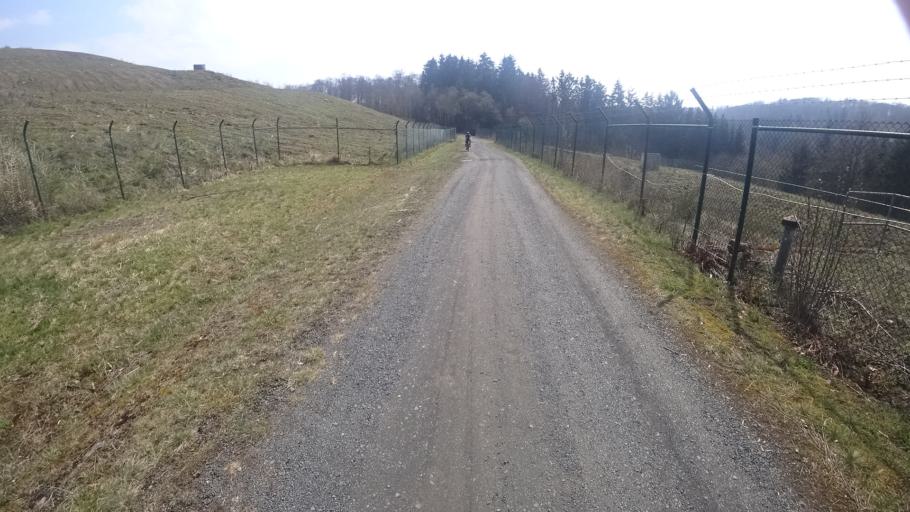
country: DE
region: Rheinland-Pfalz
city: Nauroth
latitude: 50.6927
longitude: 7.8580
